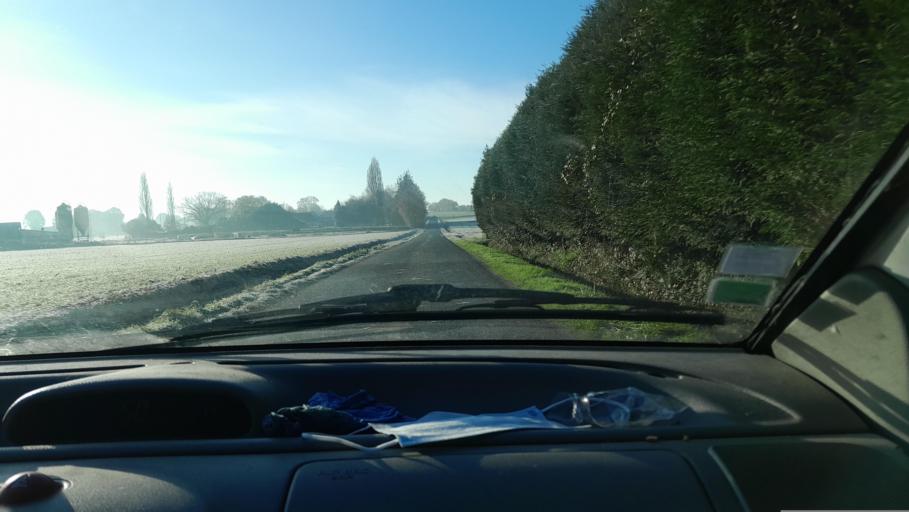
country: FR
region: Brittany
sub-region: Departement d'Ille-et-Vilaine
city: La Guerche-de-Bretagne
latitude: 47.8976
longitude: -1.1622
